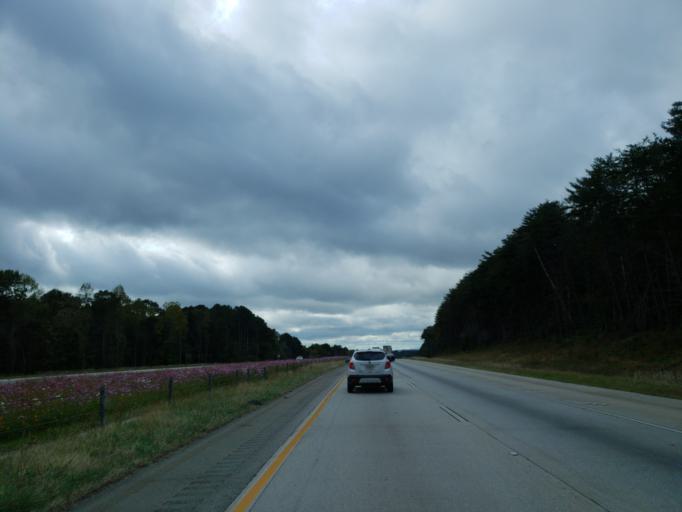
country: US
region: Georgia
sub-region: Haralson County
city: Tallapoosa
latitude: 33.6838
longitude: -85.2833
